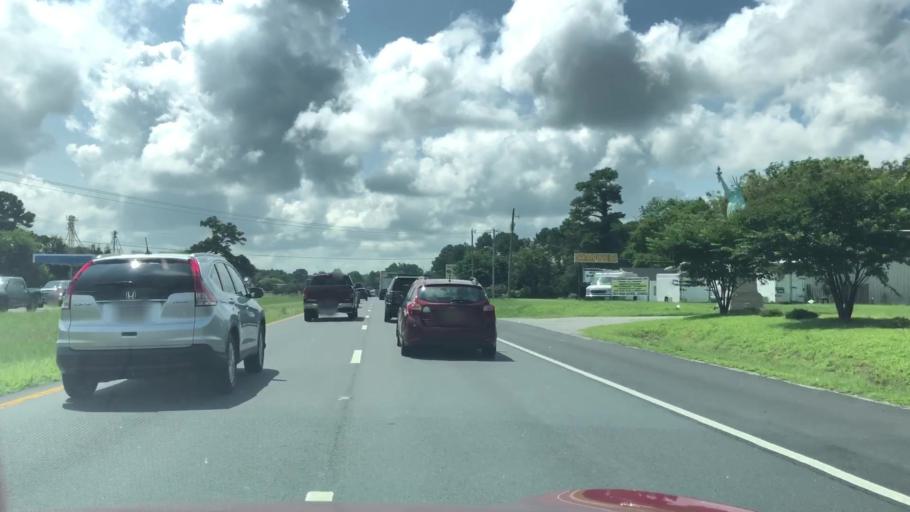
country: US
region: Virginia
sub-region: Northampton County
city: Exmore
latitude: 37.5201
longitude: -75.8320
